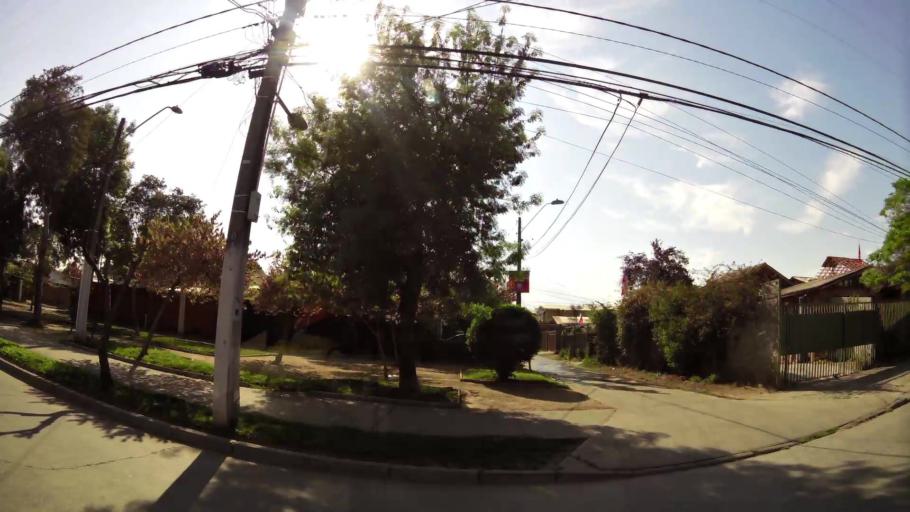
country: CL
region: Santiago Metropolitan
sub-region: Provincia de Santiago
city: La Pintana
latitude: -33.5547
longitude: -70.5986
